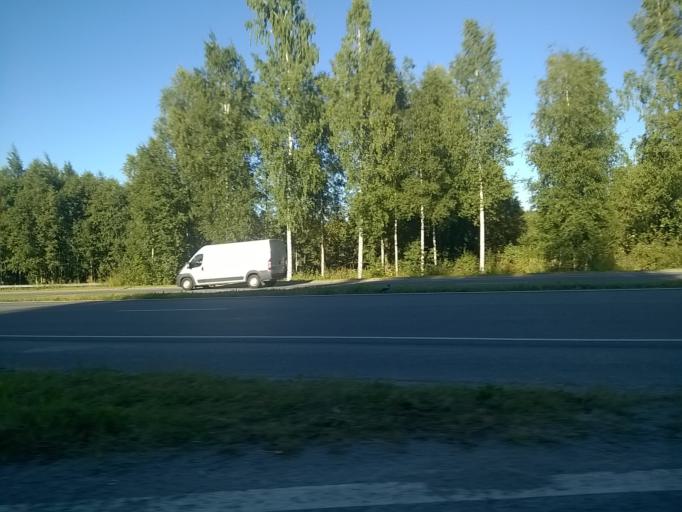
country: FI
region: Pirkanmaa
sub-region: Tampere
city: Tampere
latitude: 61.4710
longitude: 23.8399
